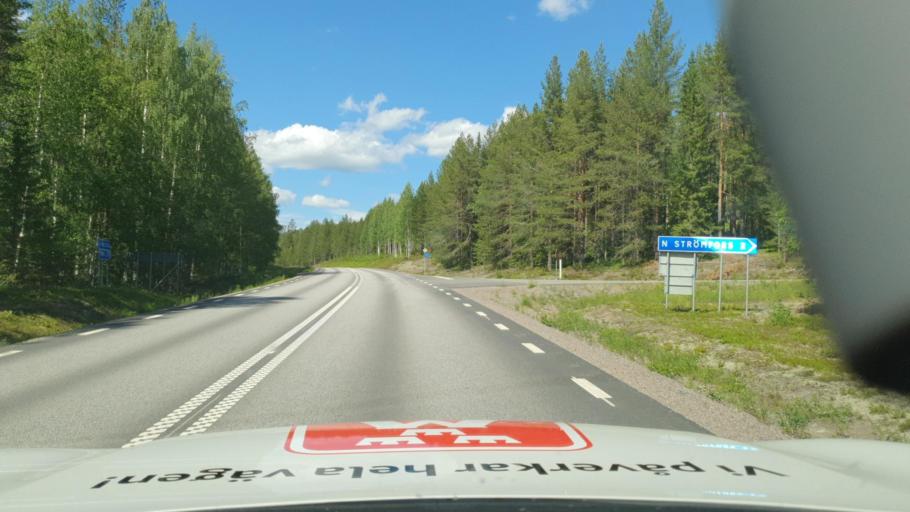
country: SE
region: Vaesterbotten
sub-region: Skelleftea Kommun
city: Boliden
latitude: 64.8993
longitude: 20.3705
